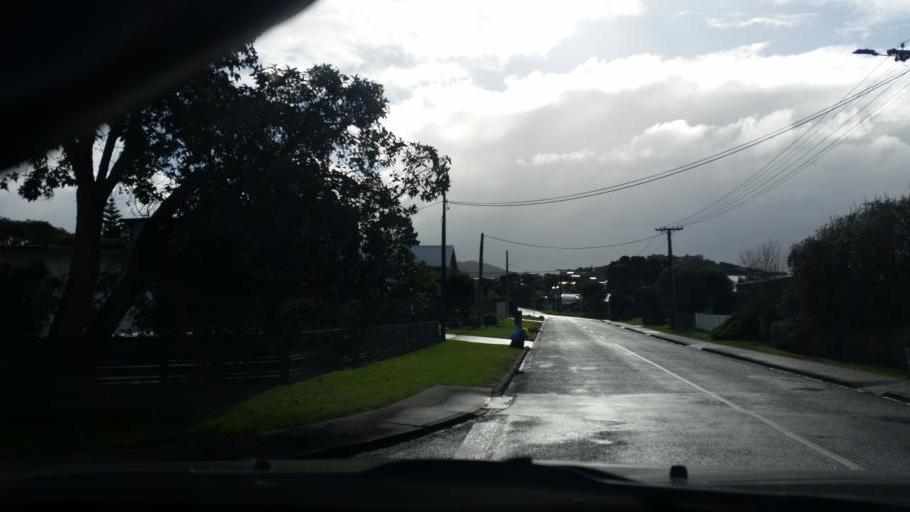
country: NZ
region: Auckland
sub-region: Auckland
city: Wellsford
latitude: -36.0913
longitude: 174.5893
